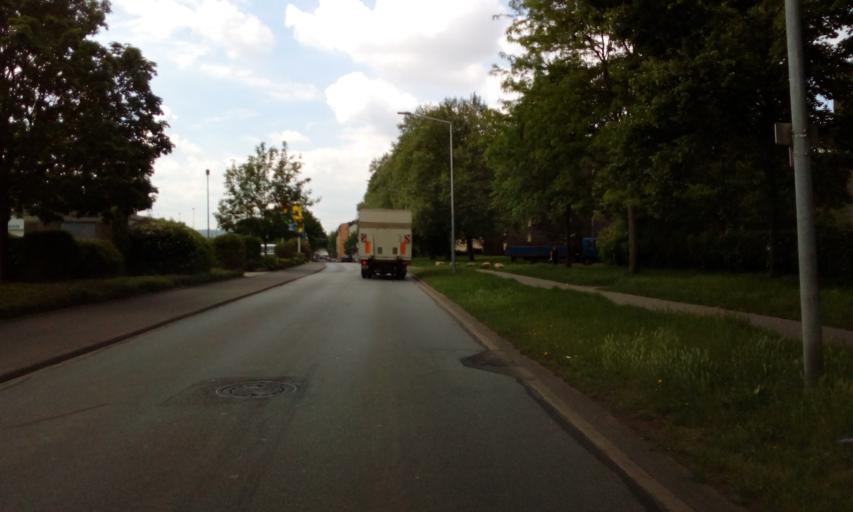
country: DE
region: Rheinland-Pfalz
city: Trier
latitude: 49.7562
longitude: 6.6232
